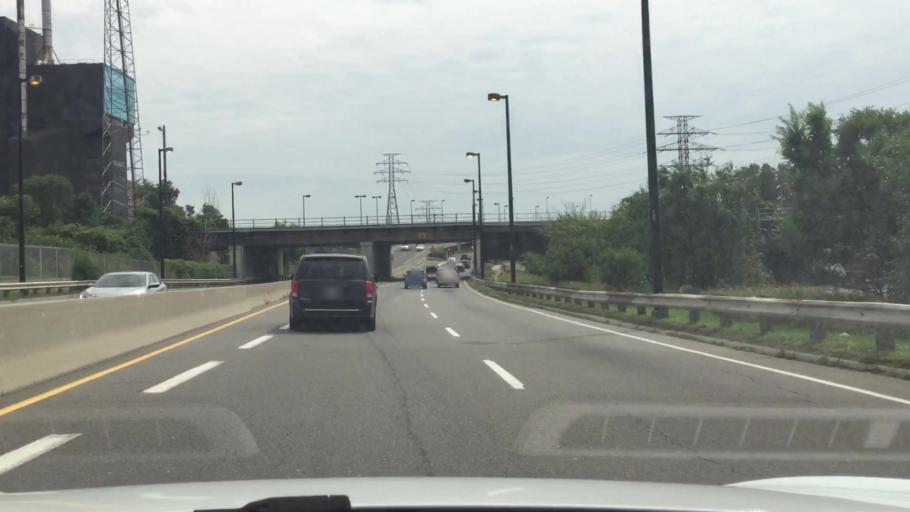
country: CA
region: Ontario
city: Toronto
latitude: 43.6545
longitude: -79.3501
